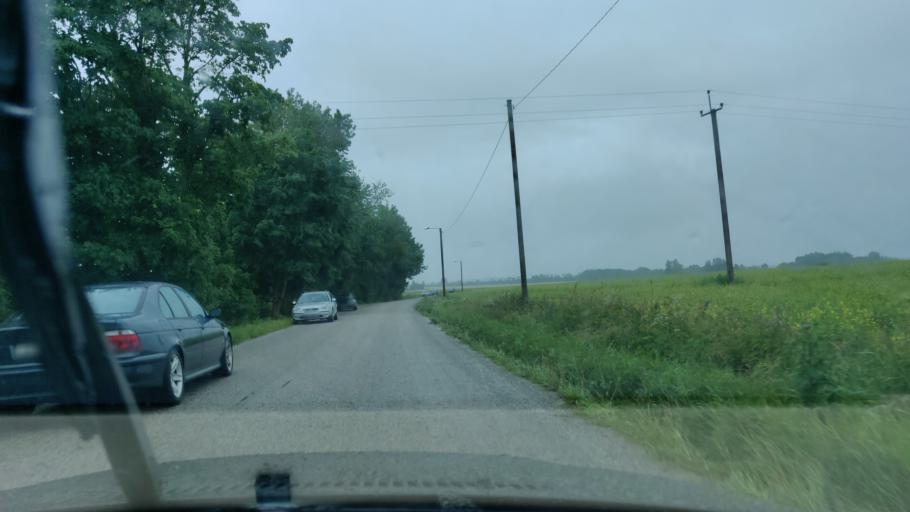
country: EE
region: Jaervamaa
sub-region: Jaerva-Jaani vald
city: Jarva-Jaani
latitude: 59.0946
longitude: 25.6992
